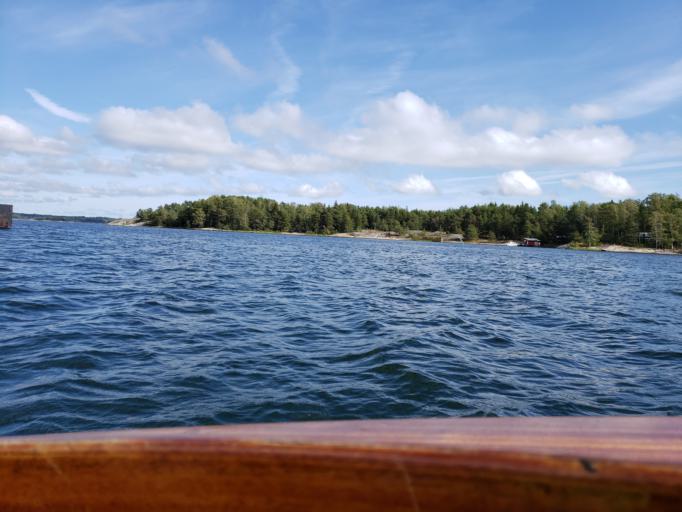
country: FI
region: Varsinais-Suomi
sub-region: Aboland-Turunmaa
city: Dragsfjaerd
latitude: 59.9206
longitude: 22.4116
